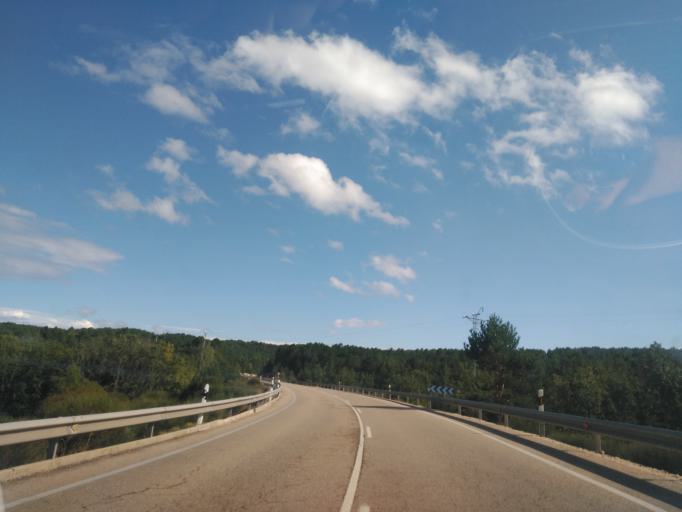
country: ES
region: Castille and Leon
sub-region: Provincia de Burgos
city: Pinilla de los Barruecos
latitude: 41.9154
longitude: -3.2790
